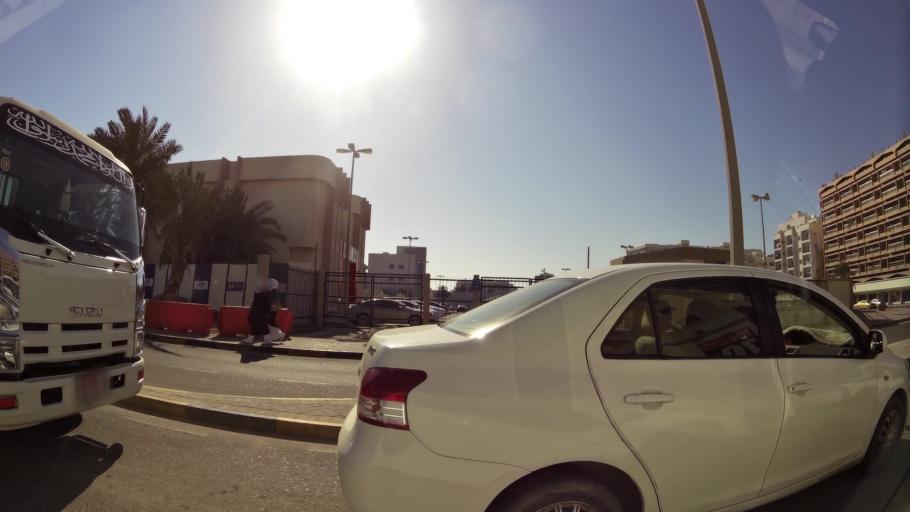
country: BH
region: Manama
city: Manama
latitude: 26.2189
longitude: 50.5739
